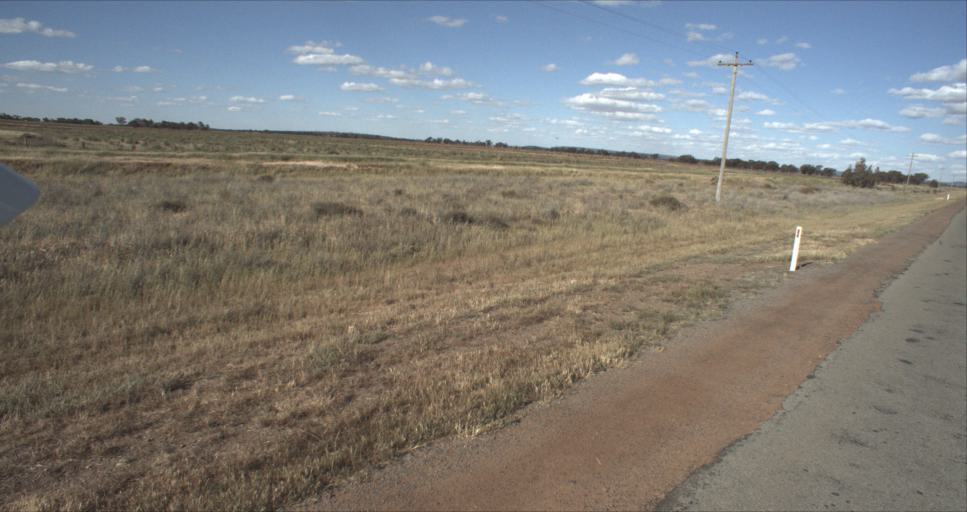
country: AU
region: New South Wales
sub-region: Leeton
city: Leeton
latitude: -34.4552
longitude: 146.2761
